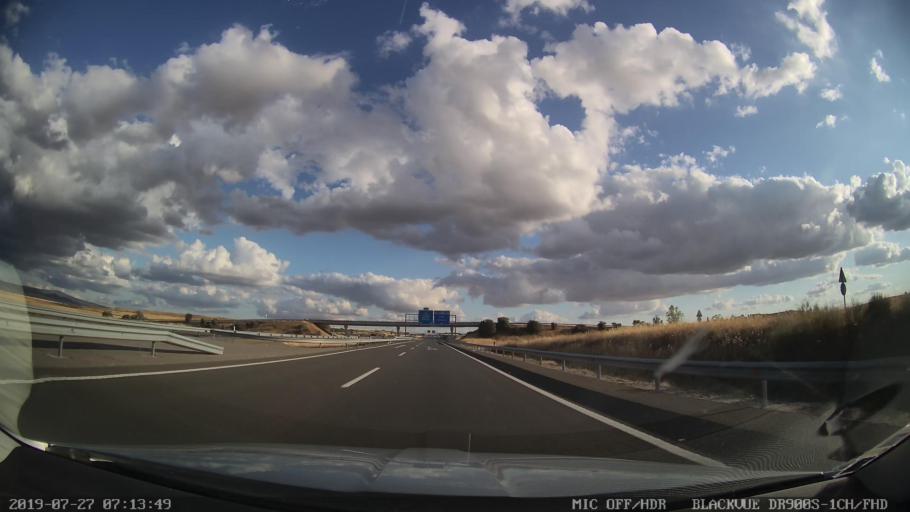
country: ES
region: Extremadura
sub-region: Provincia de Caceres
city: Trujillo
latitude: 39.5046
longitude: -5.8390
